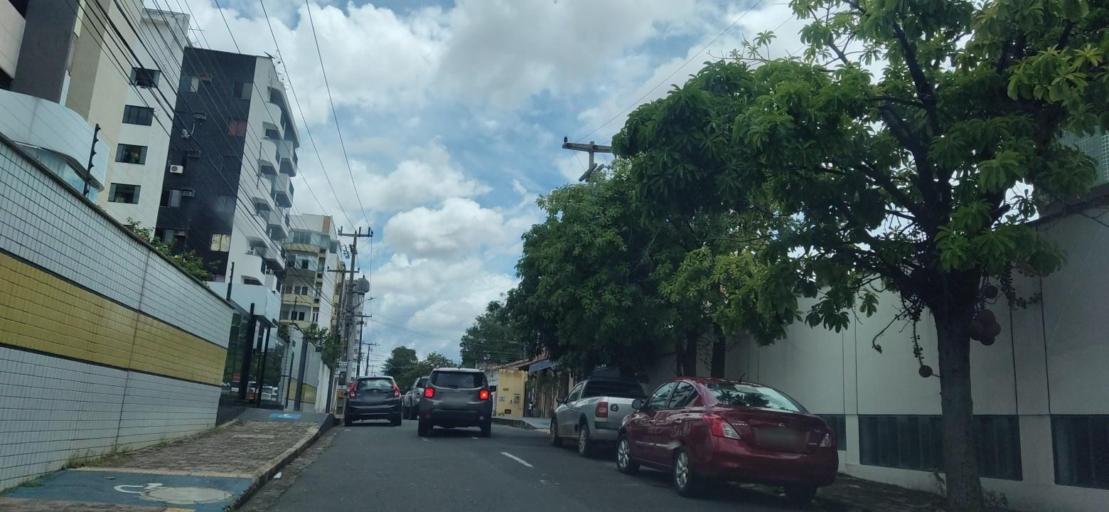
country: BR
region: Piaui
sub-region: Teresina
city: Teresina
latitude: -5.0853
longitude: -42.7984
